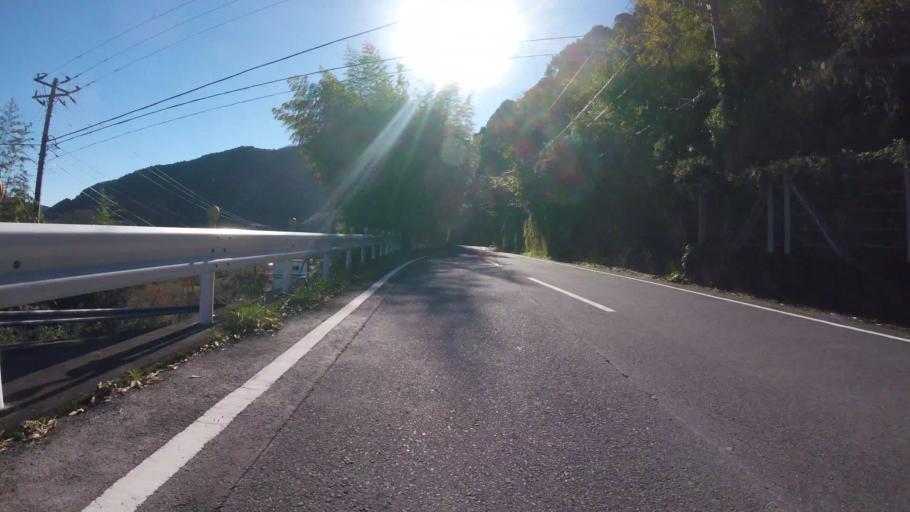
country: JP
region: Shizuoka
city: Shimoda
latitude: 34.7711
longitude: 138.9588
